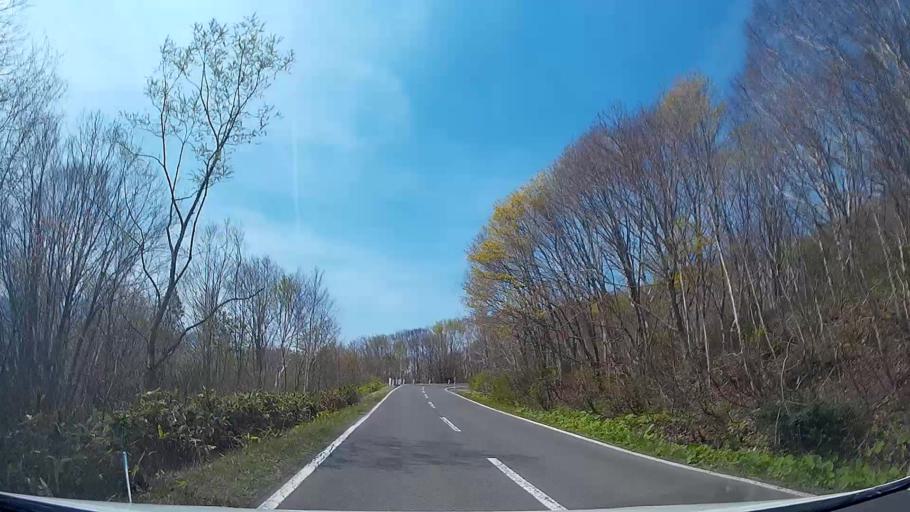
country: JP
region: Iwate
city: Shizukuishi
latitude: 39.9338
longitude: 140.9568
